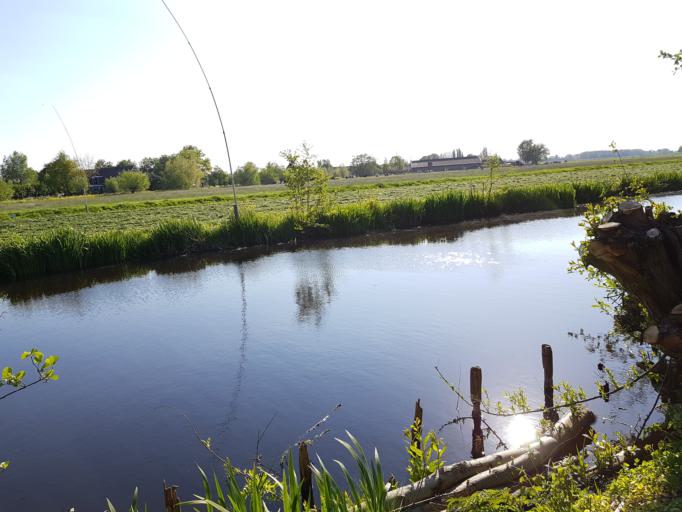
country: NL
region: South Holland
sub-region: Gemeente Vlist
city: Vlist
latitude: 51.9768
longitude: 4.7993
